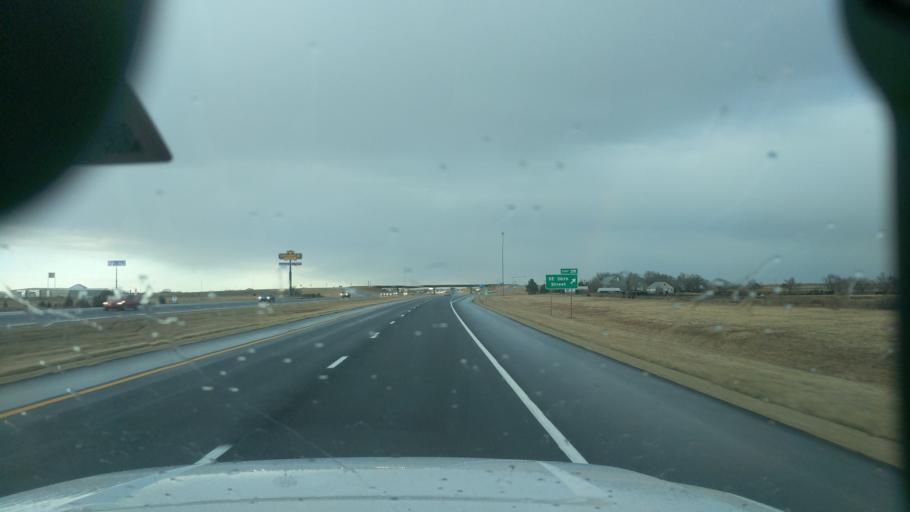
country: US
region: Kansas
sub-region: Harvey County
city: Newton
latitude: 37.9944
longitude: -97.3280
